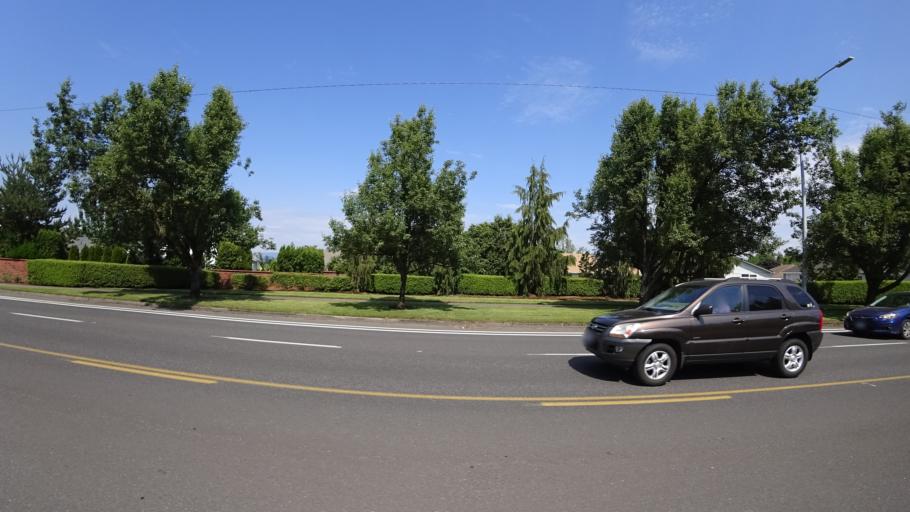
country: US
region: Oregon
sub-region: Multnomah County
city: Fairview
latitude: 45.5349
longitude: -122.5096
